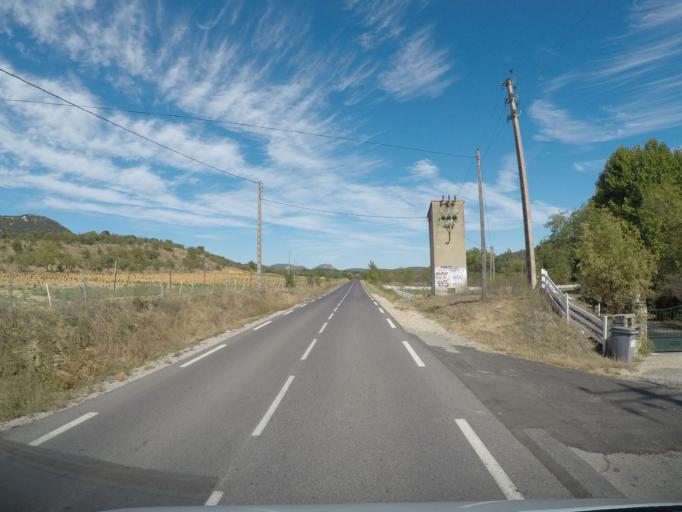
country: FR
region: Languedoc-Roussillon
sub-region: Departement de l'Herault
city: Saint-Bauzille-de-Putois
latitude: 43.9122
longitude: 3.7737
